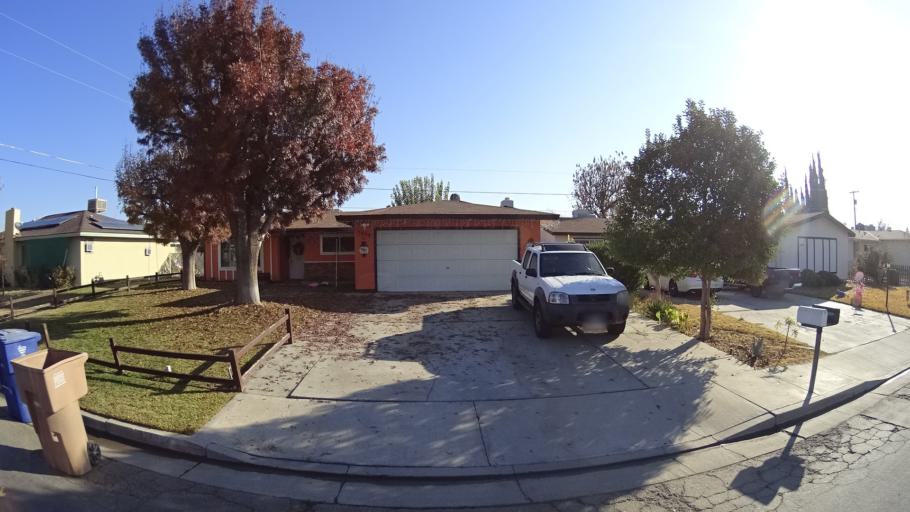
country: US
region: California
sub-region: Kern County
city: Greenfield
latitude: 35.3018
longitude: -119.0177
